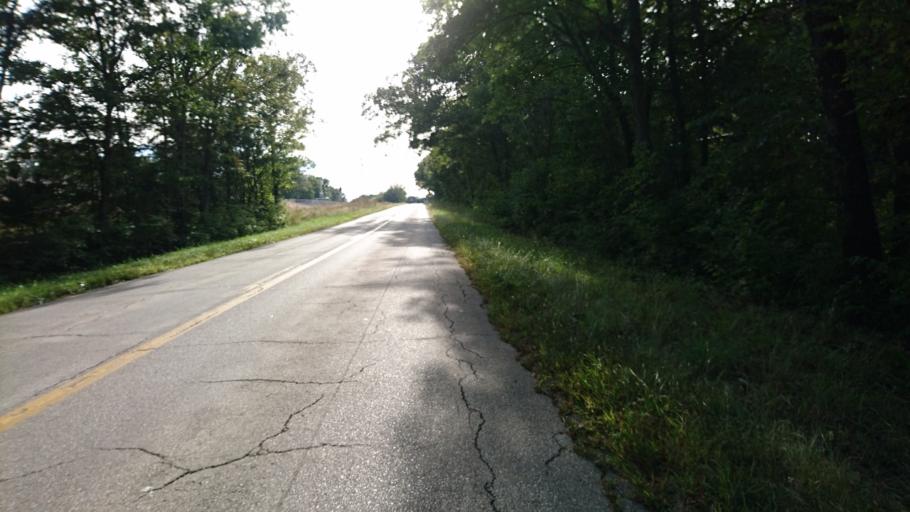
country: US
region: Missouri
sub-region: Crawford County
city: Cuba
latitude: 38.0969
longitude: -91.3590
